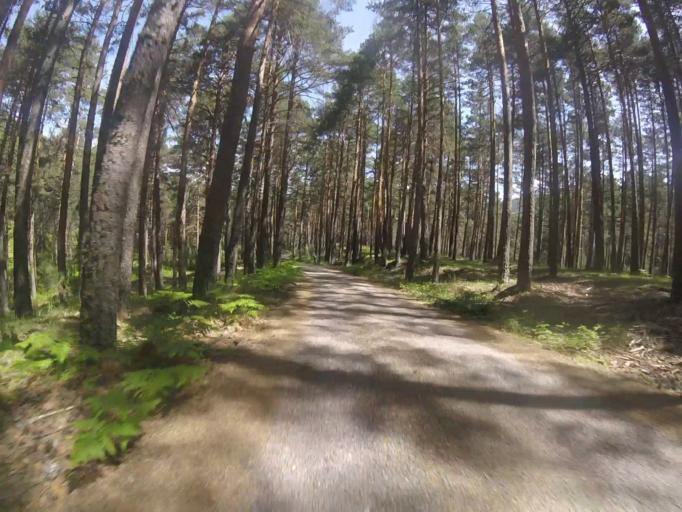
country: ES
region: Madrid
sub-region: Provincia de Madrid
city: Cercedilla
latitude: 40.8175
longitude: -4.0289
